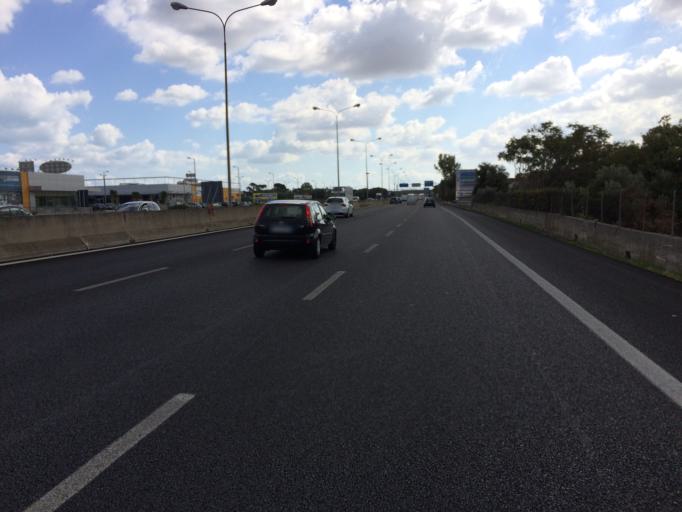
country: IT
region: Apulia
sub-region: Provincia di Bari
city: Bari
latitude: 41.0952
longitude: 16.8327
